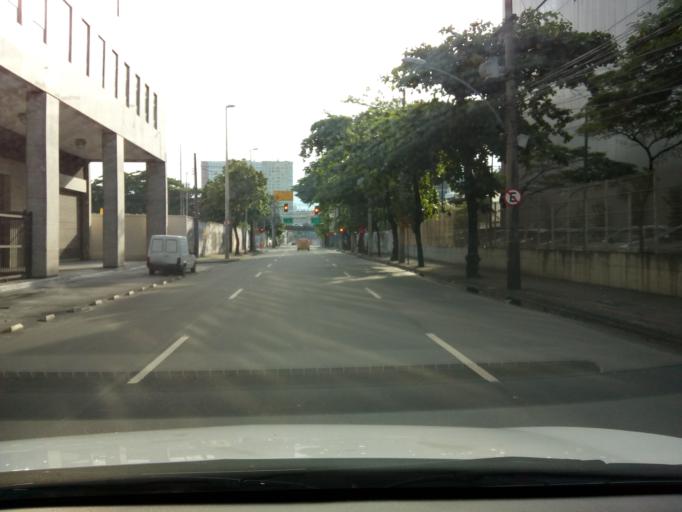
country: BR
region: Rio de Janeiro
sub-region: Rio De Janeiro
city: Rio de Janeiro
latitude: -22.9091
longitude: -43.1995
